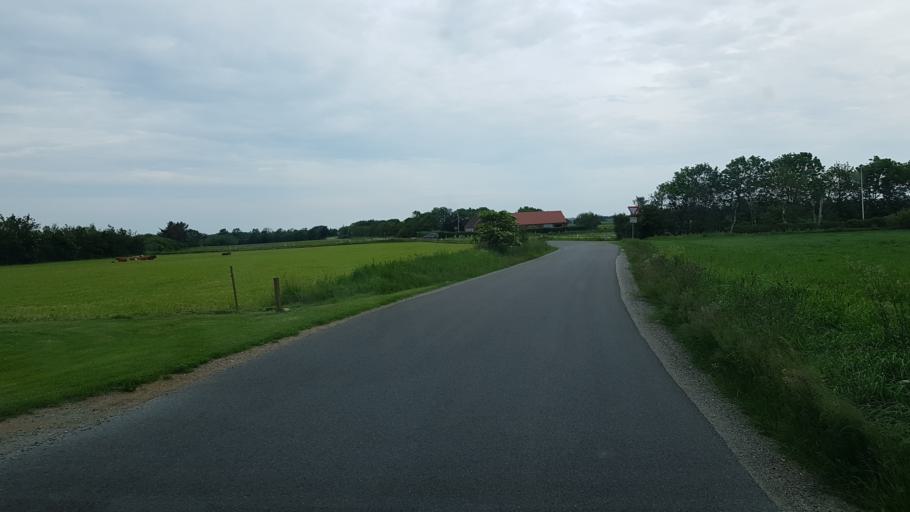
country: DK
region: South Denmark
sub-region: Varde Kommune
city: Oksbol
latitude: 55.7229
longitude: 8.3707
